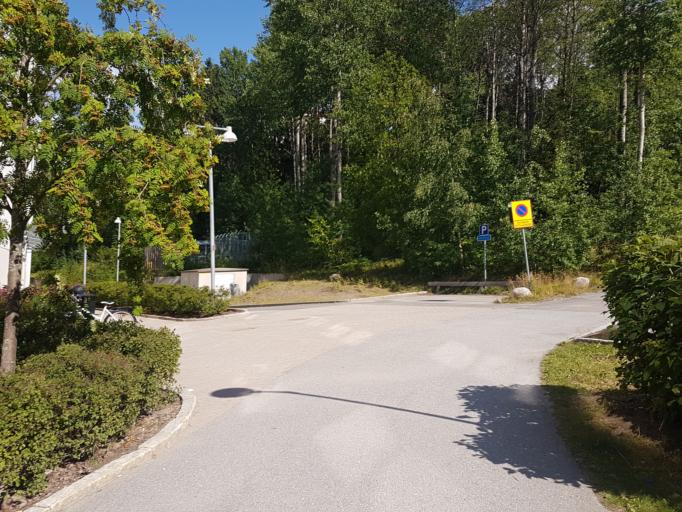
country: SE
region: Stockholm
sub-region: Huddinge Kommun
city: Huddinge
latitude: 59.2170
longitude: 17.9482
